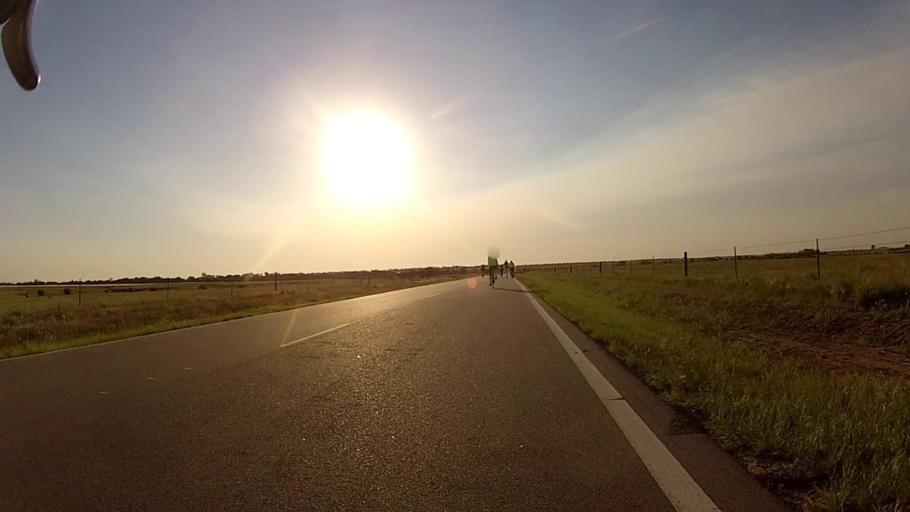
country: US
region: Kansas
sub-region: Harper County
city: Anthony
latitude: 37.1545
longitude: -97.8084
